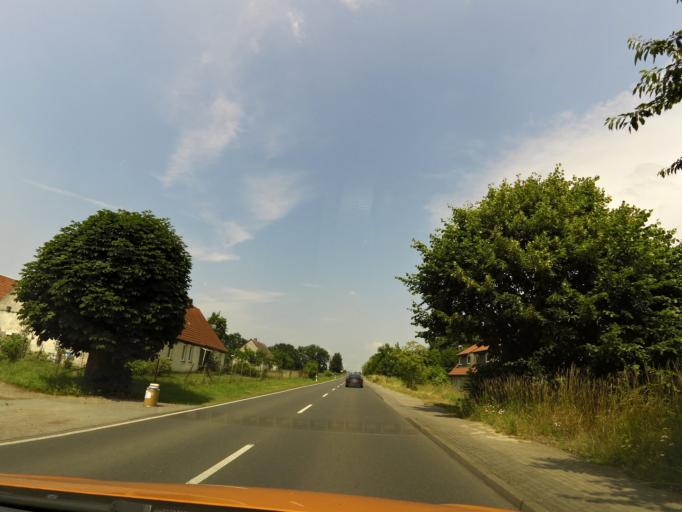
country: DE
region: Brandenburg
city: Pritzwalk
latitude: 53.1949
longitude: 12.1988
